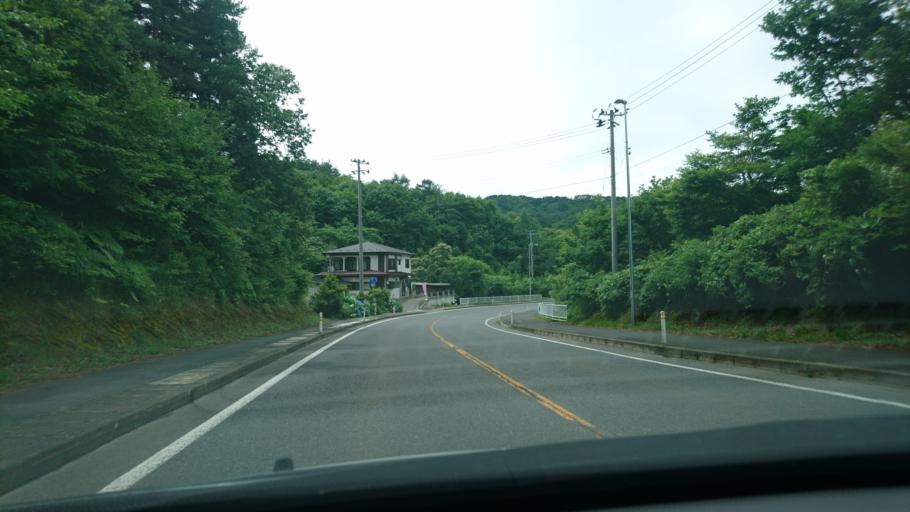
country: JP
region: Iwate
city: Miyako
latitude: 39.9297
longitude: 141.8953
